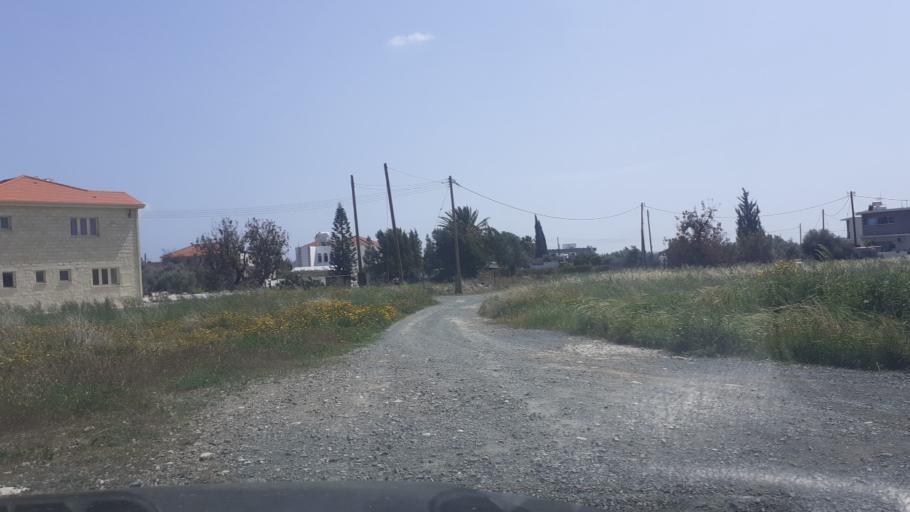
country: CY
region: Limassol
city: Ypsonas
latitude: 34.6862
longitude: 32.9516
